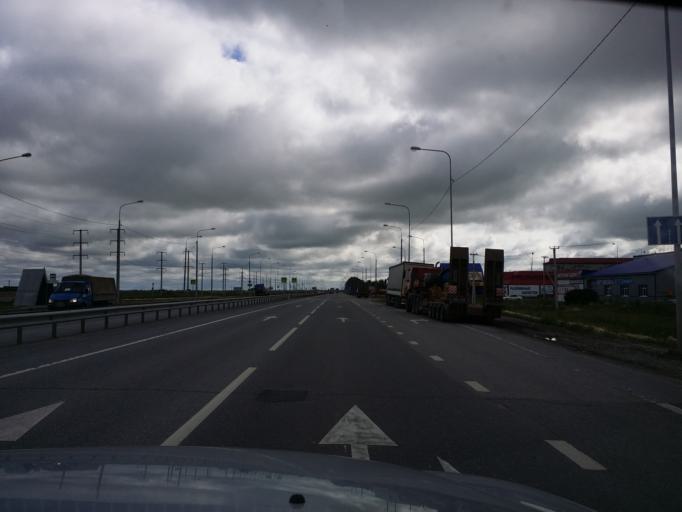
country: RU
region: Tjumen
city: Antipino
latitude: 57.1792
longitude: 65.9254
